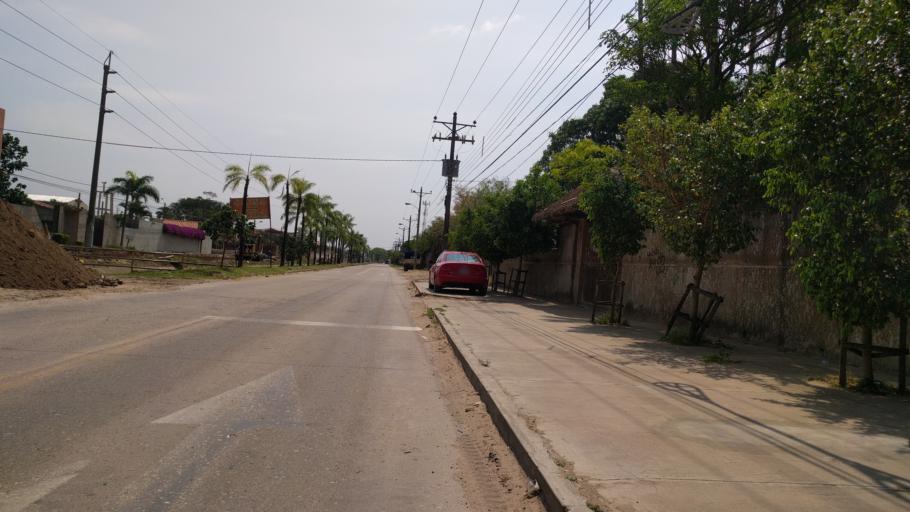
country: BO
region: Santa Cruz
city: Santa Cruz de la Sierra
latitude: -17.8257
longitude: -63.2141
